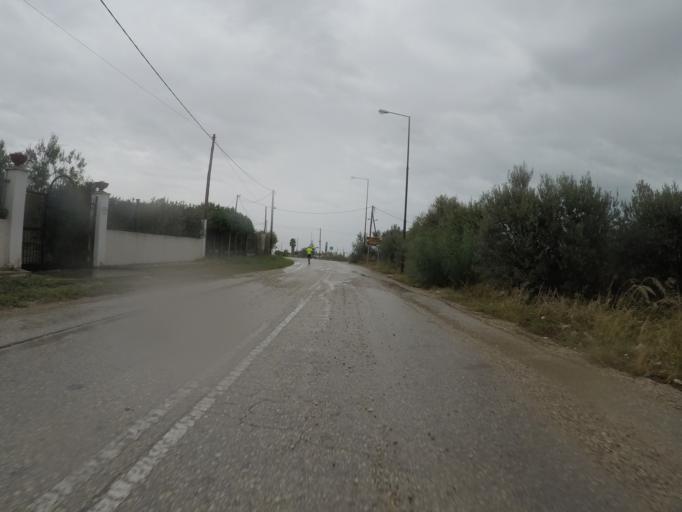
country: GR
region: Peloponnese
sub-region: Nomos Korinthias
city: Arkhaia Korinthos
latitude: 37.9009
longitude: 22.8885
